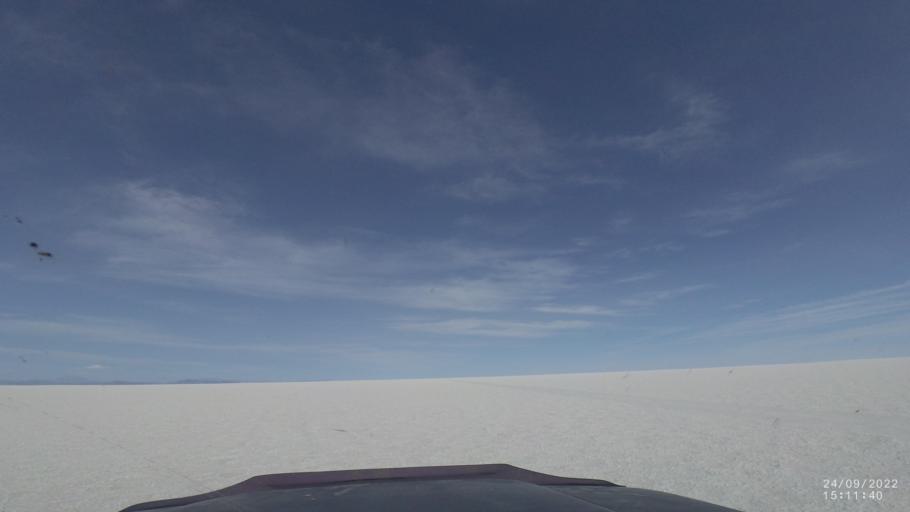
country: BO
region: Potosi
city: Colchani
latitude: -19.9461
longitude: -67.4756
